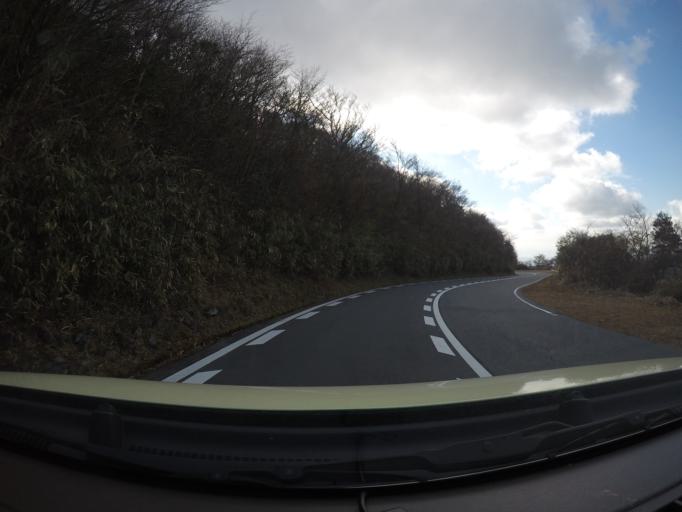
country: JP
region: Kanagawa
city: Hakone
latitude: 35.2107
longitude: 138.9877
